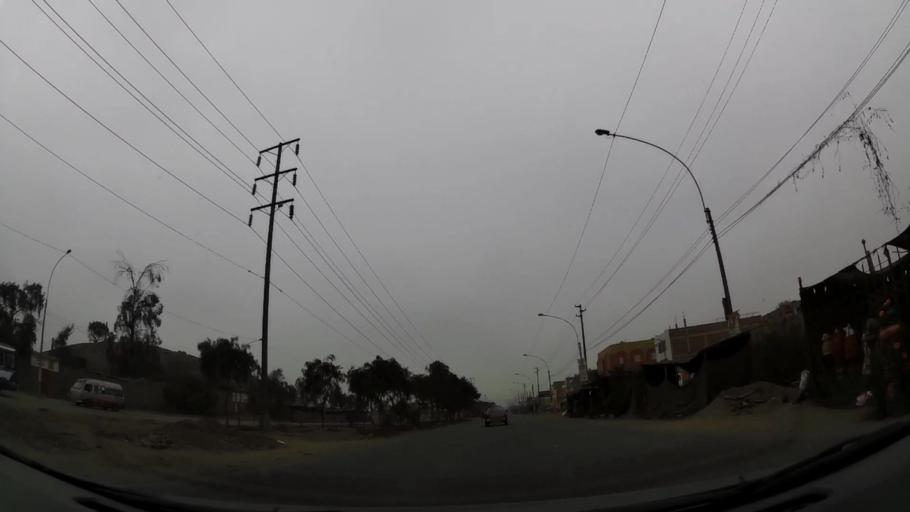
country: PE
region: Lima
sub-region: Lima
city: Urb. Santo Domingo
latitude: -11.9077
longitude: -77.0544
